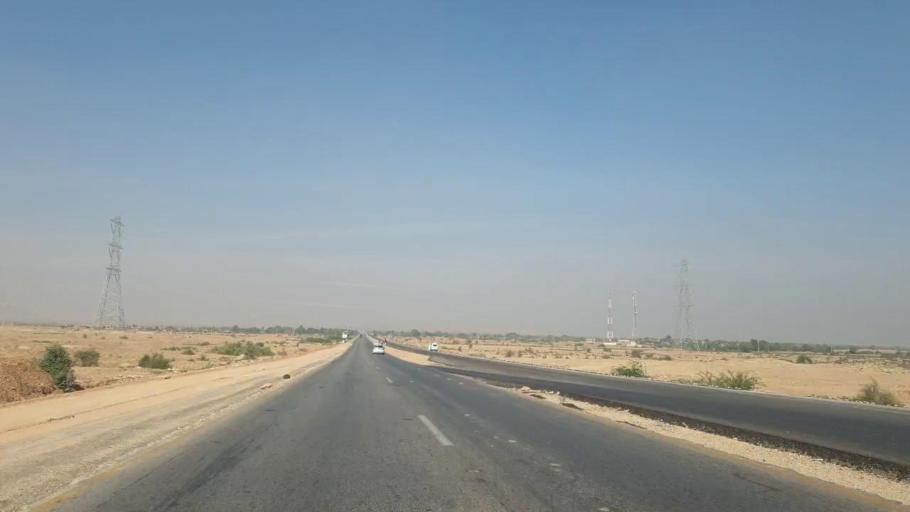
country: PK
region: Sindh
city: Matiari
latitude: 25.5848
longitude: 68.3114
